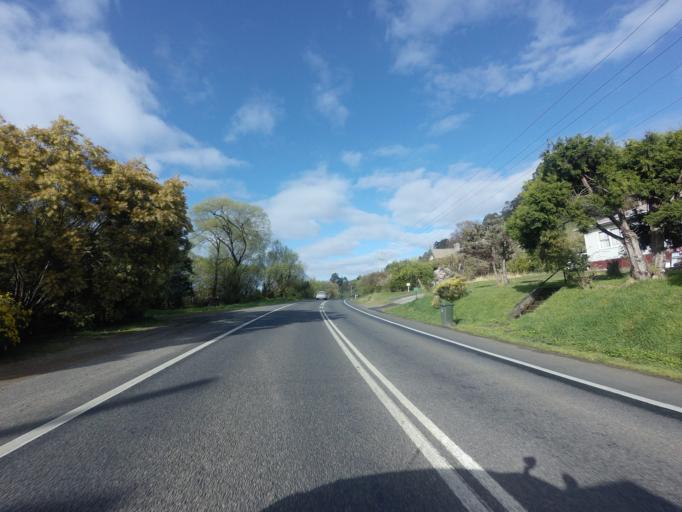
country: AU
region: Tasmania
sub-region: Huon Valley
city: Franklin
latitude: -43.0991
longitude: 147.0051
